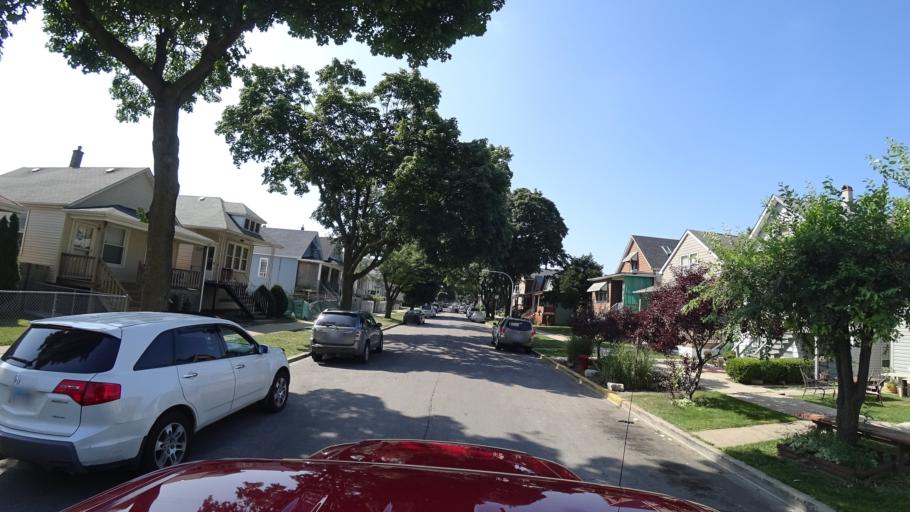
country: US
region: Illinois
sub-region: Cook County
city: Chicago
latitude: 41.8223
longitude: -87.6861
